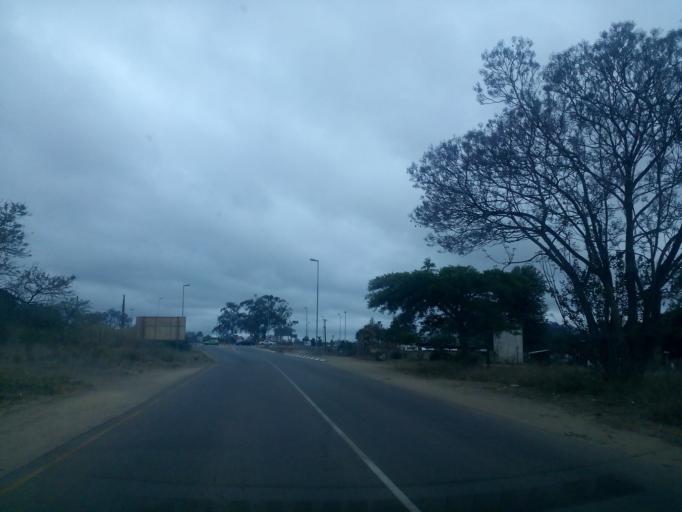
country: ZA
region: Limpopo
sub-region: Vhembe District Municipality
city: Louis Trichardt
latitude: -23.0784
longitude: 29.9073
